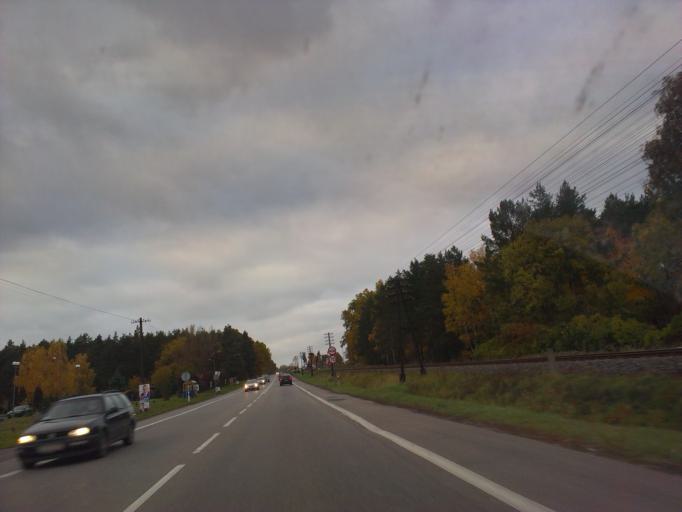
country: PL
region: Kujawsko-Pomorskie
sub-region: Powiat torunski
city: Lysomice
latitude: 53.0698
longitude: 18.6176
